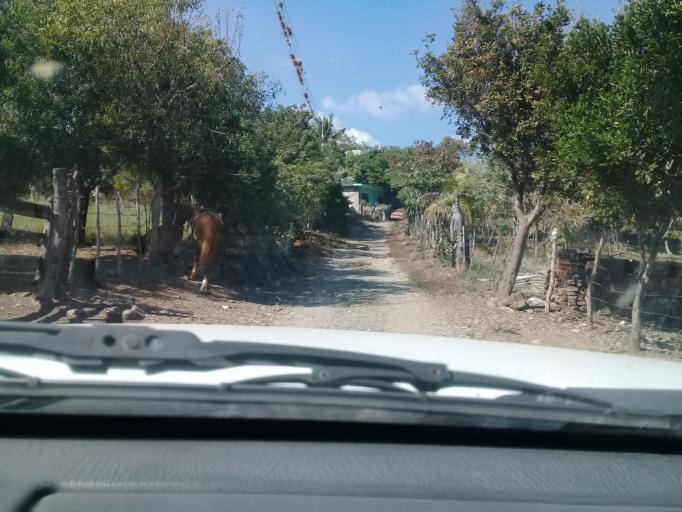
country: MX
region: Veracruz
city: Actopan
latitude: 19.4806
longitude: -96.6465
